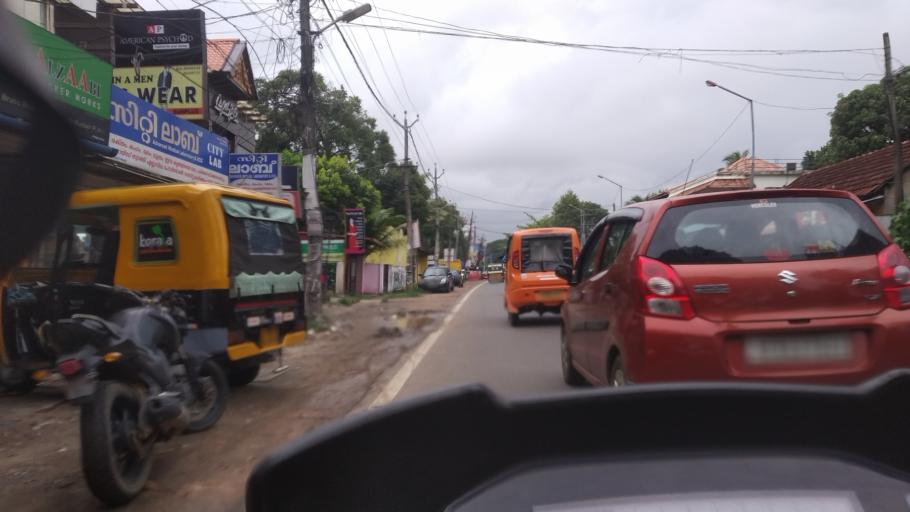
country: IN
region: Kerala
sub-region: Alappuzha
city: Alleppey
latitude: 9.4860
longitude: 76.3378
